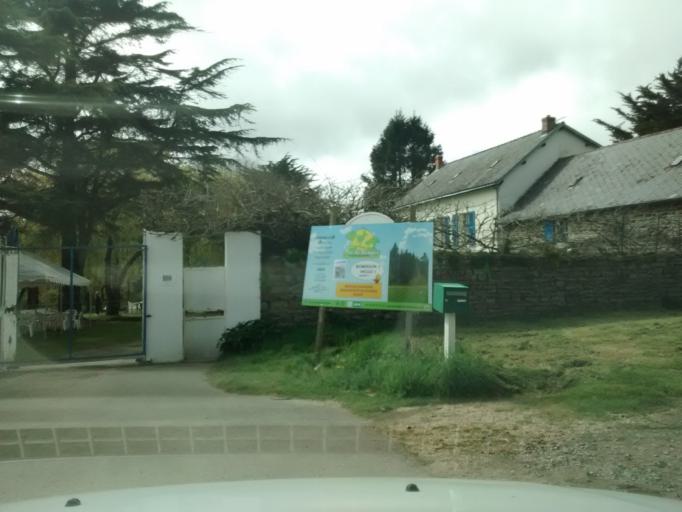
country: FR
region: Brittany
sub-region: Departement du Finistere
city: Clohars-Carnoet
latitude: 47.7864
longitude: -3.5529
